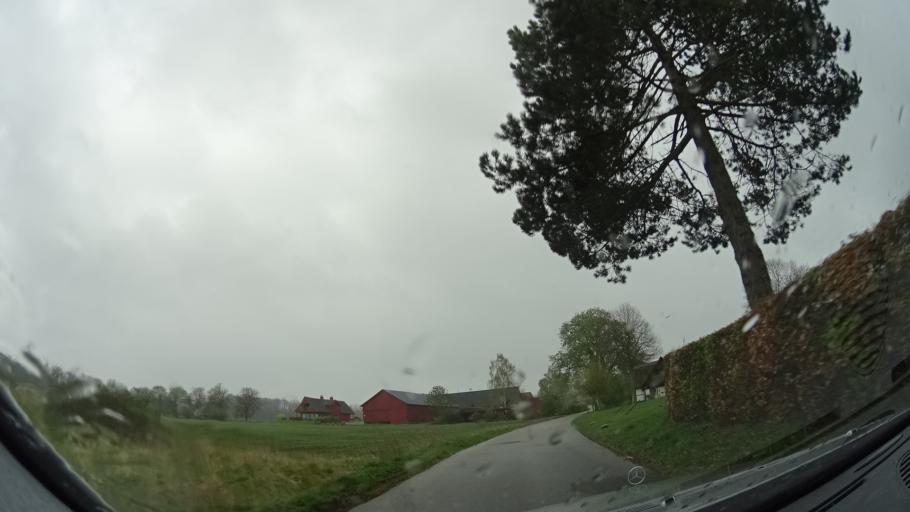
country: DK
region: Zealand
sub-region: Holbaek Kommune
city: Holbaek
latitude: 55.7192
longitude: 11.7723
